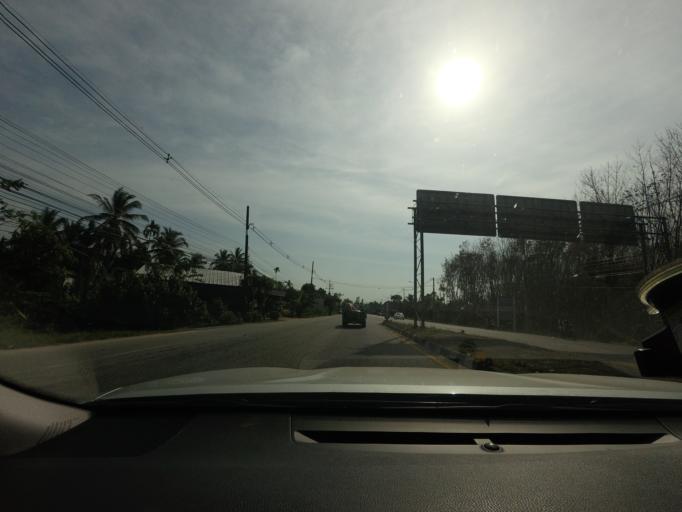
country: TH
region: Narathiwat
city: Narathiwat
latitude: 6.3812
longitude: 101.8042
